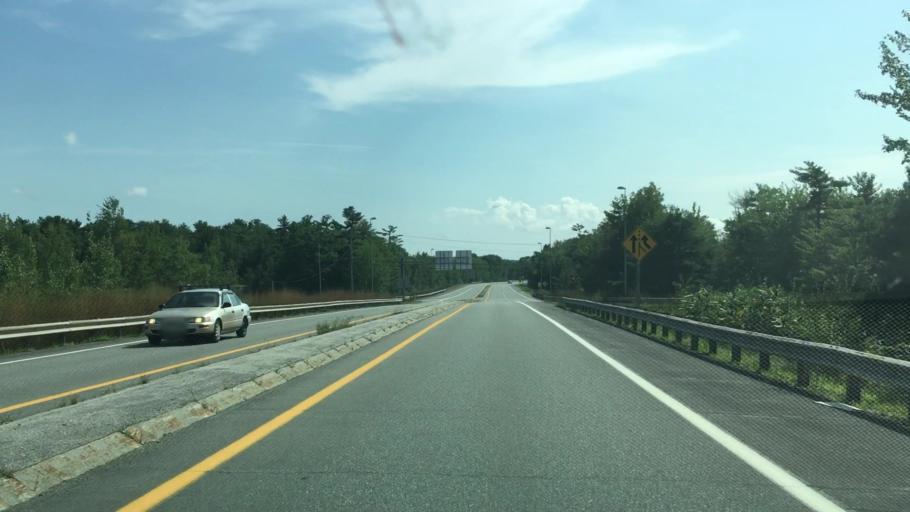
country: US
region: Maine
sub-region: Penobscot County
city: Bangor
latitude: 44.7857
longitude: -68.7944
